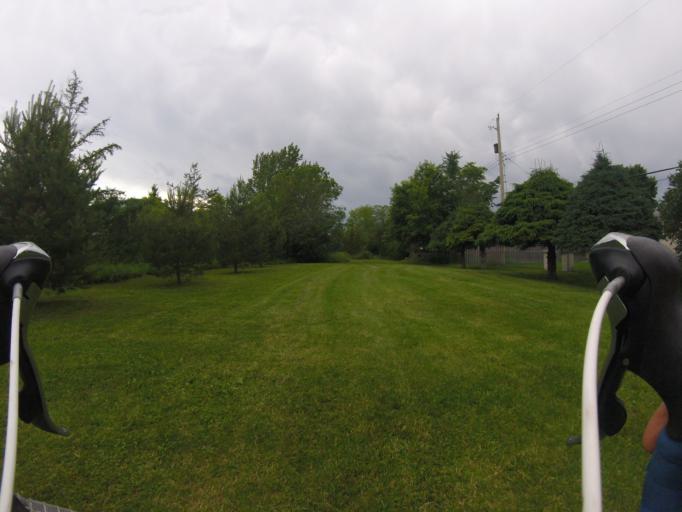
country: CA
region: Ontario
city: Ottawa
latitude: 45.3399
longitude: -75.7403
